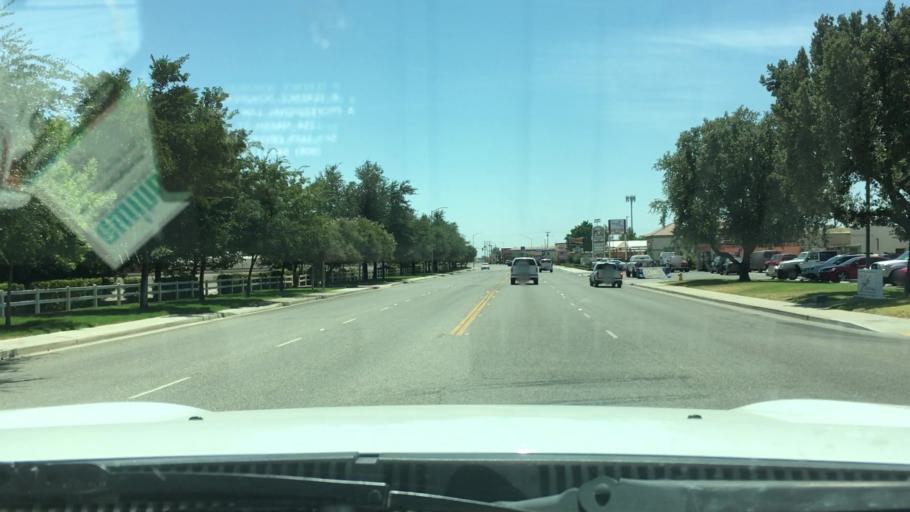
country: US
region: California
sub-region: Kern County
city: Shafter
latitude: 35.5021
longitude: -119.2735
